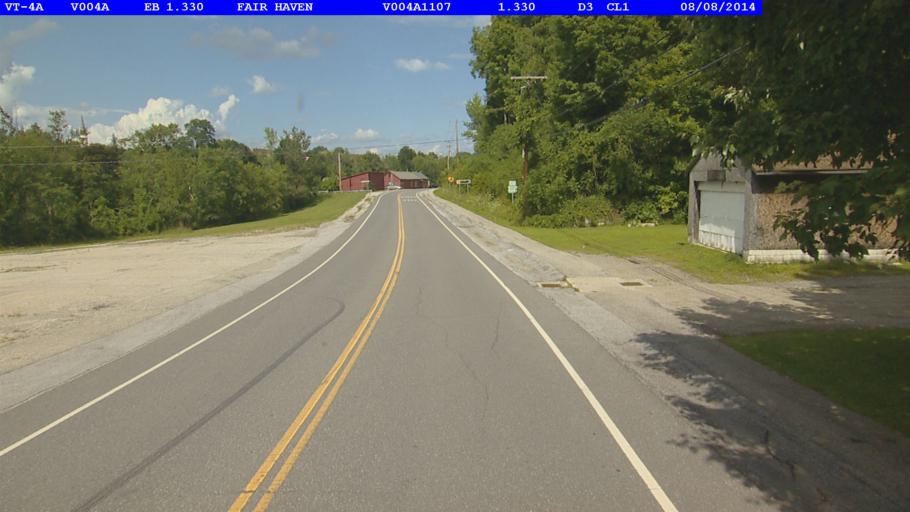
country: US
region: Vermont
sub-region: Rutland County
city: Fair Haven
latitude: 43.5883
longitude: -73.2677
